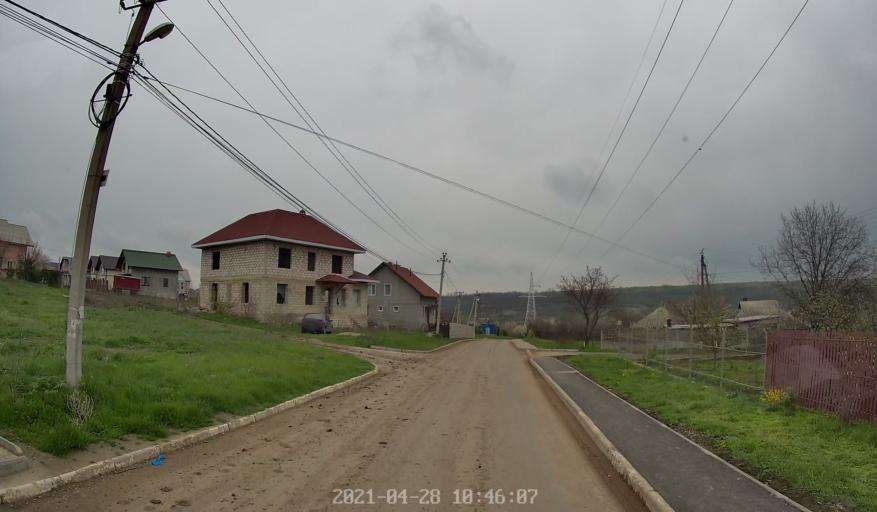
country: MD
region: Chisinau
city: Singera
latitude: 46.9897
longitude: 28.9425
